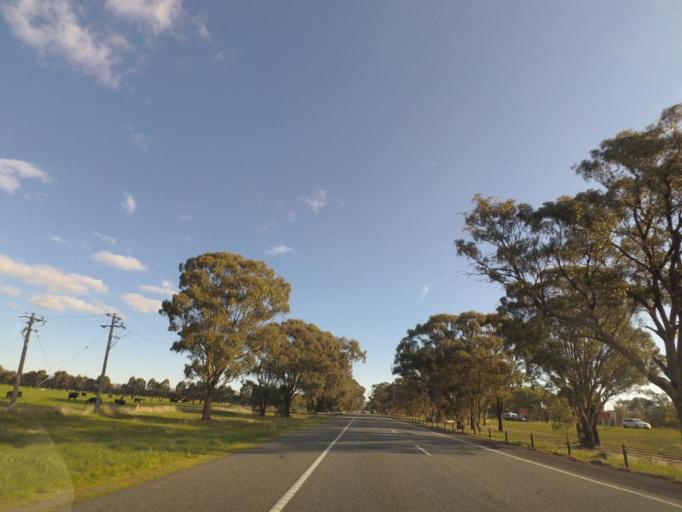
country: AU
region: Victoria
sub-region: Benalla
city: Benalla
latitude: -36.6915
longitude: 145.6617
